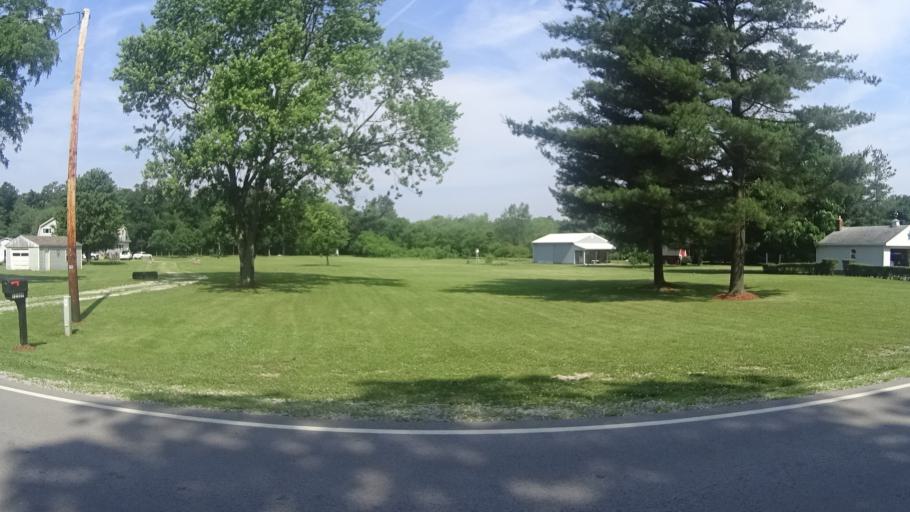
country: US
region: Ohio
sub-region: Huron County
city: Monroeville
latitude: 41.3003
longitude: -82.7134
